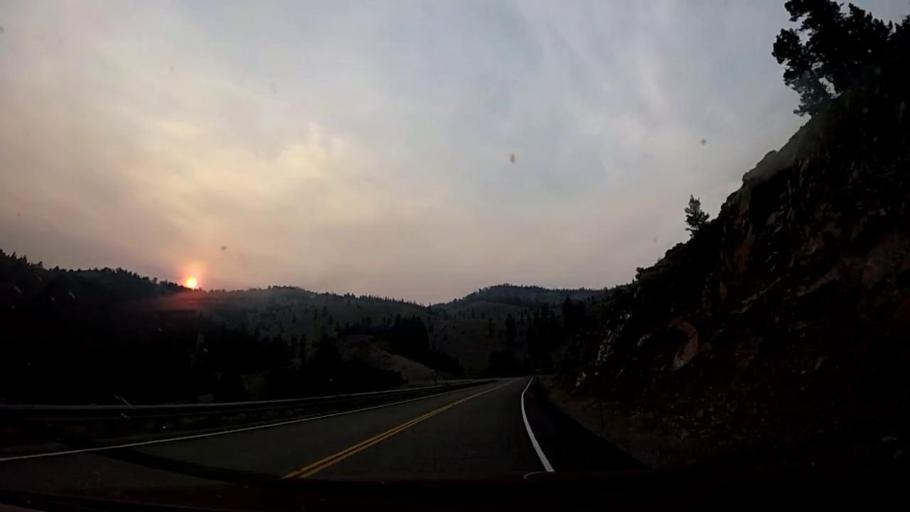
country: US
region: Idaho
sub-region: Blaine County
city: Ketchum
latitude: 43.8857
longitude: -114.6930
